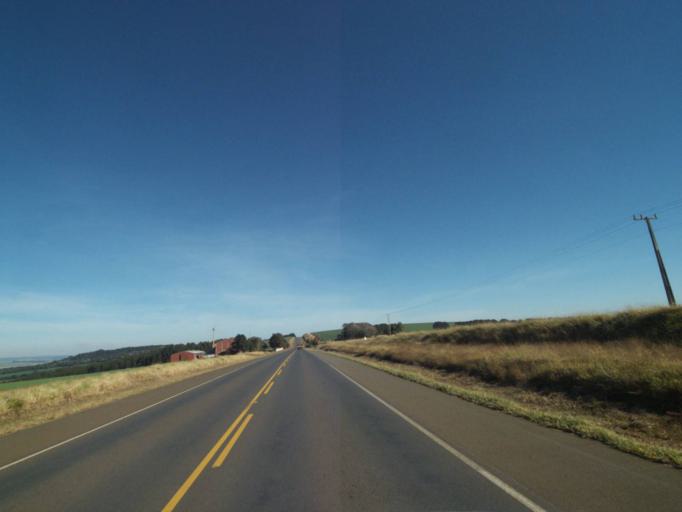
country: BR
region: Parana
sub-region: Tibagi
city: Tibagi
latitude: -24.3563
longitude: -50.3173
